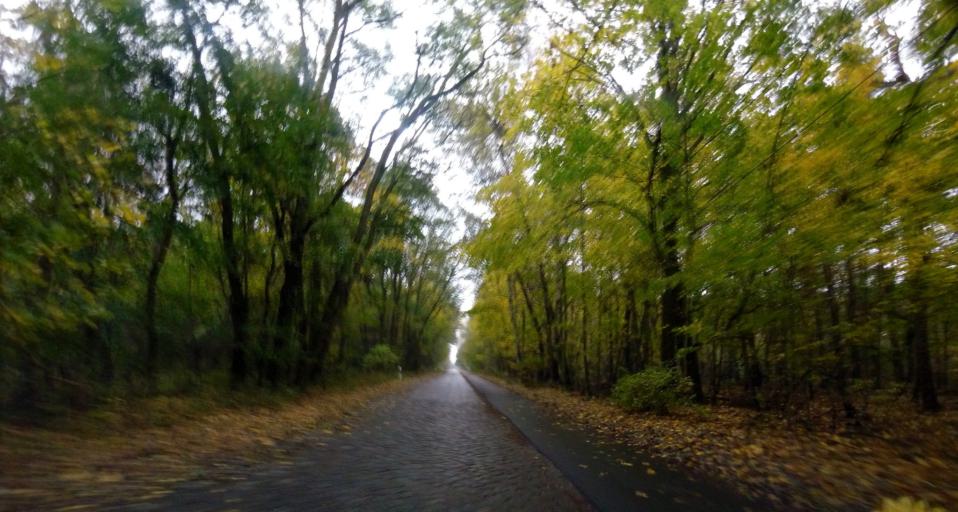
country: DE
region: Brandenburg
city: Niedergorsdorf
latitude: 51.9996
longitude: 12.9723
